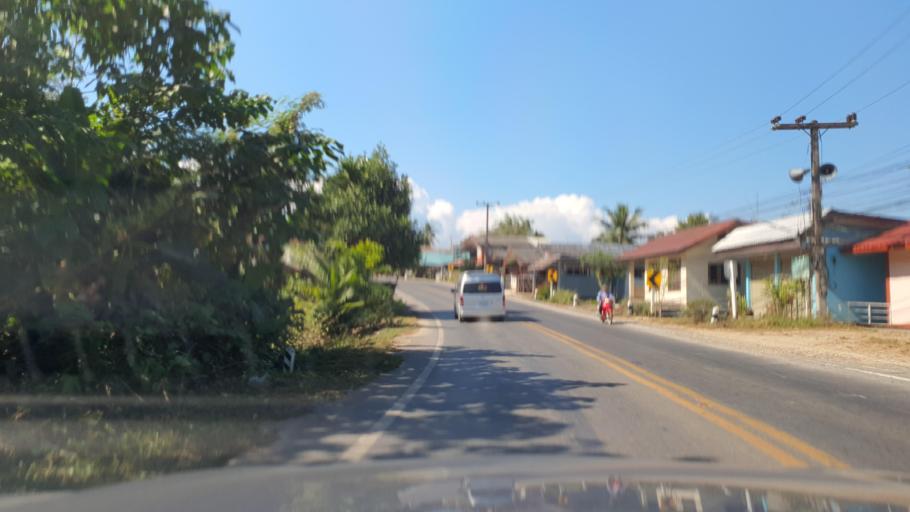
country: TH
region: Nan
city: Tha Wang Pha
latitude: 19.1062
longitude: 100.8124
